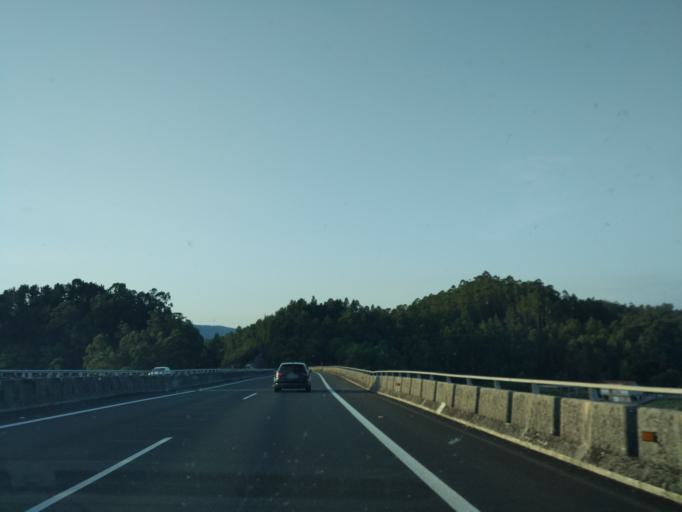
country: ES
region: Galicia
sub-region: Provincia de Pontevedra
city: Portas
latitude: 42.5754
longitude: -8.6731
